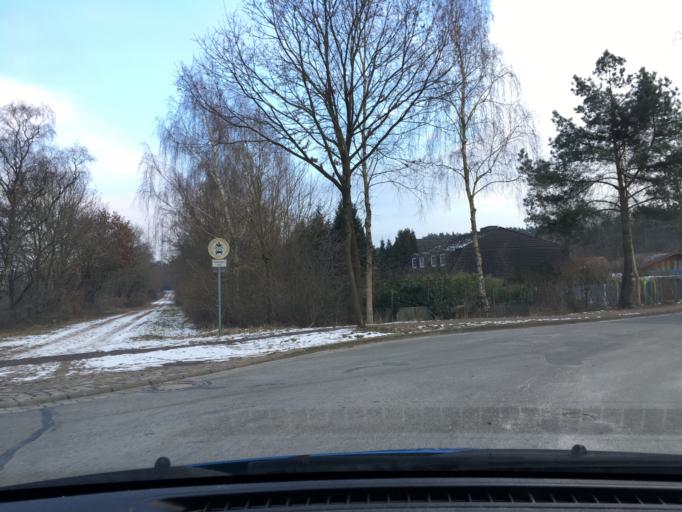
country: DE
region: Lower Saxony
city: Bienenbuttel
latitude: 53.1531
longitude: 10.4826
